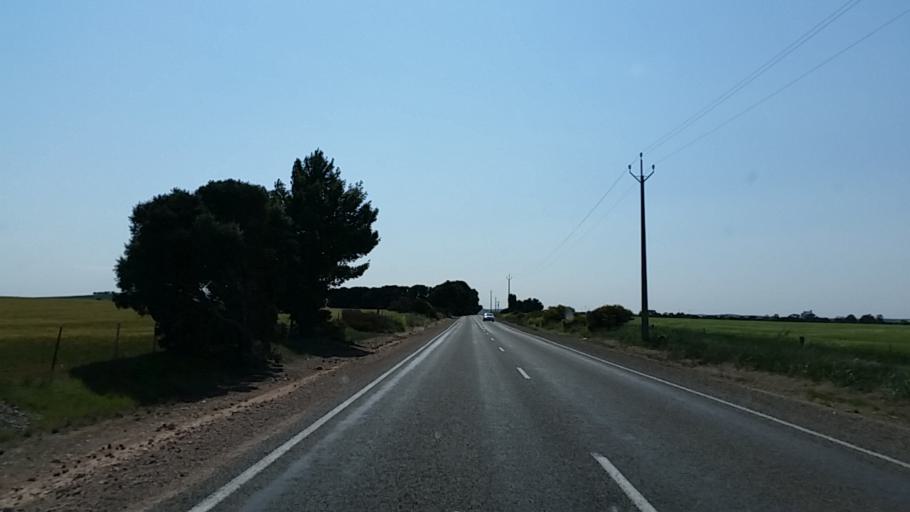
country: AU
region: South Australia
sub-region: Northern Areas
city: Jamestown
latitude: -33.1896
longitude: 138.4622
